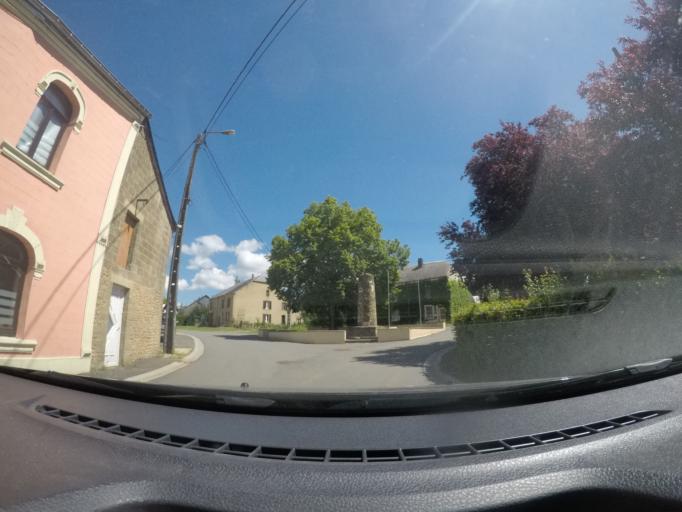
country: BE
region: Wallonia
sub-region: Province du Luxembourg
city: Tintigny
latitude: 49.6708
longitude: 5.5355
